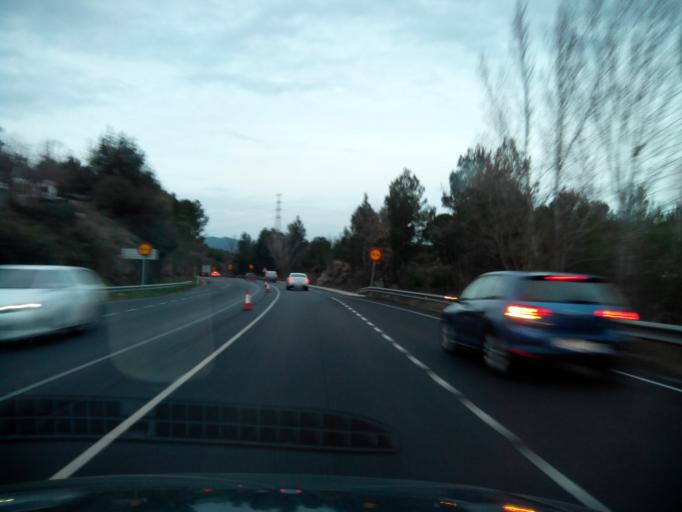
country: ES
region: Catalonia
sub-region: Provincia de Barcelona
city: Monistrol de Montserrat
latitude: 41.6008
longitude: 1.8912
